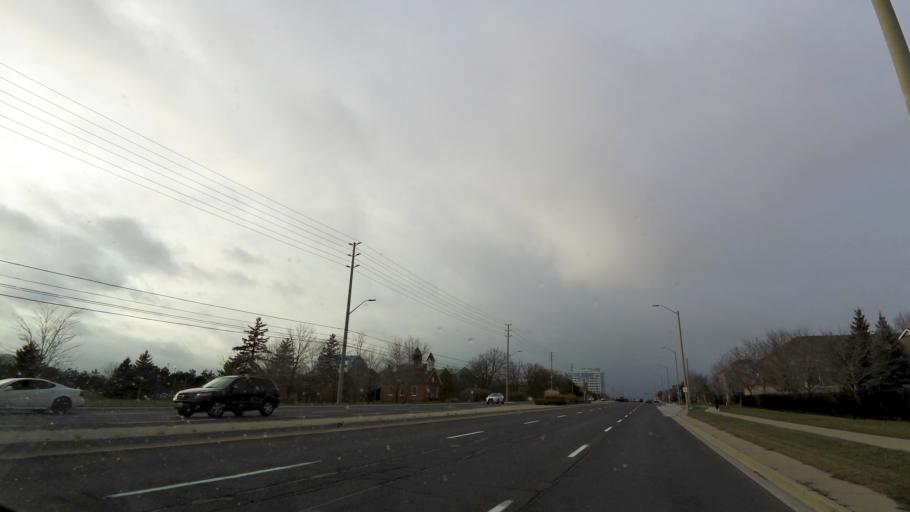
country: CA
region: Ontario
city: Mississauga
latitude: 43.6174
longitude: -79.6672
